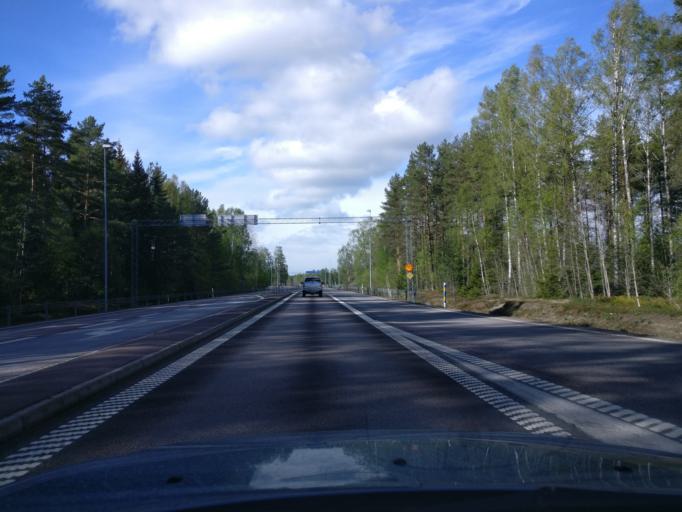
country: SE
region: Vaermland
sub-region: Forshaga Kommun
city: Forshaga
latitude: 59.4554
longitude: 13.4168
